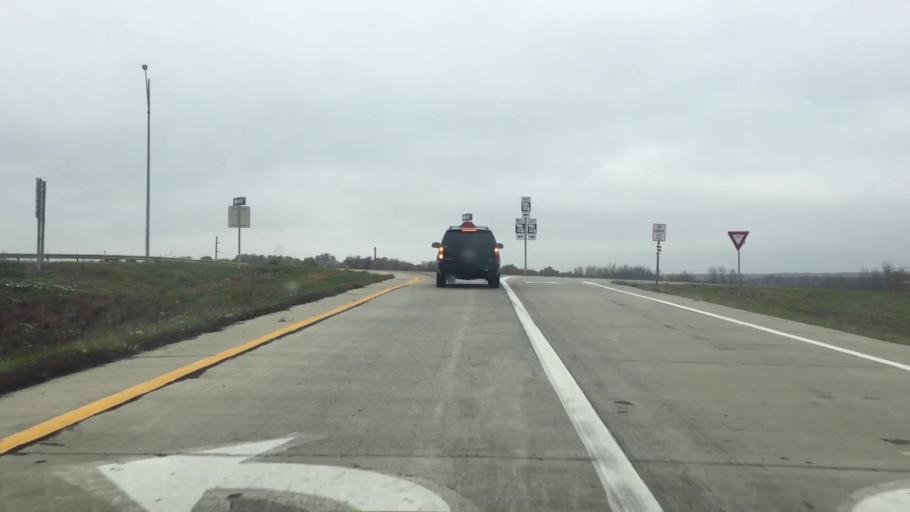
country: US
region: Missouri
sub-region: Saint Clair County
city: Osceola
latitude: 38.0405
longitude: -93.6803
